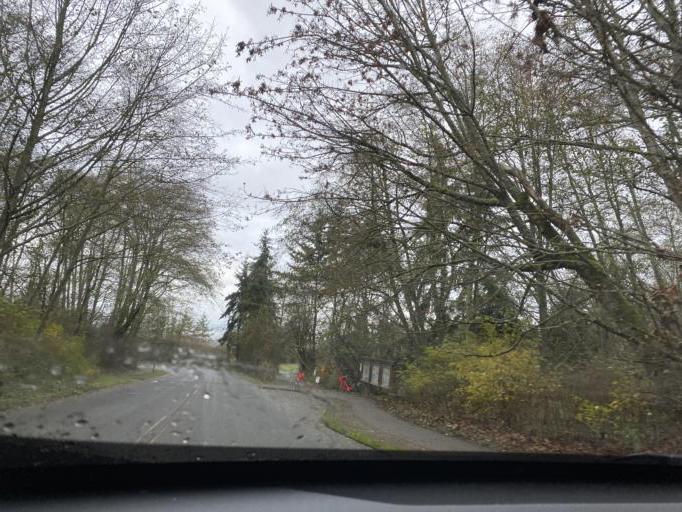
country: US
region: Washington
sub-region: Kitsap County
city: Bainbridge Island
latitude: 47.6602
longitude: -122.4278
